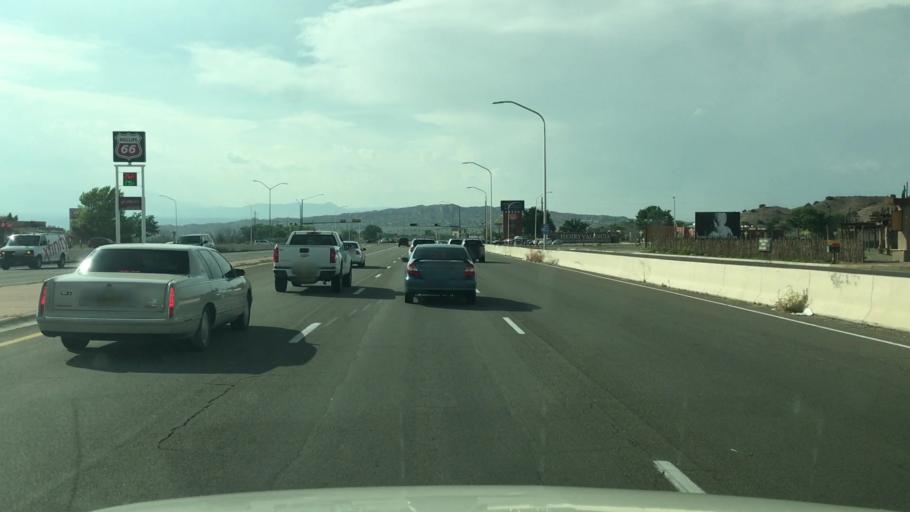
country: US
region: New Mexico
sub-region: Santa Fe County
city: Pojoaque
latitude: 35.8813
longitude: -106.0121
